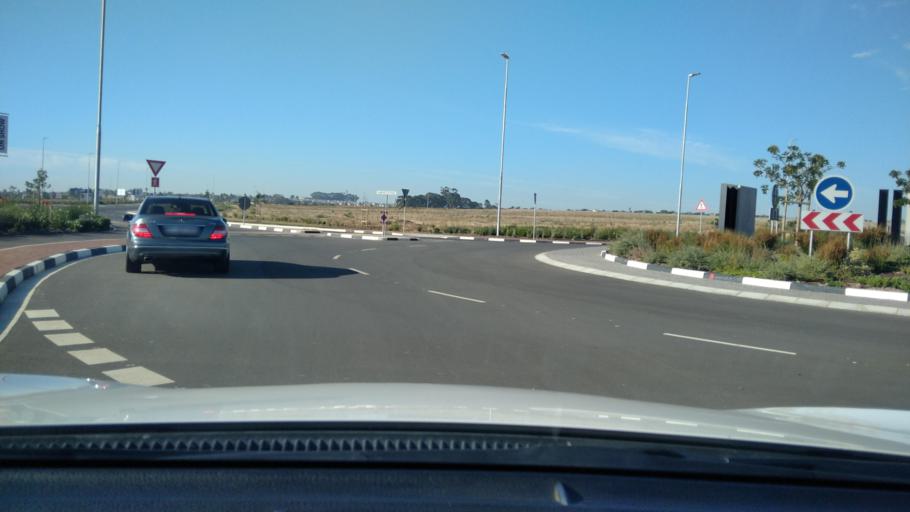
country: ZA
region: Western Cape
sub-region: City of Cape Town
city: Kraaifontein
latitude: -33.8084
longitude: 18.6892
